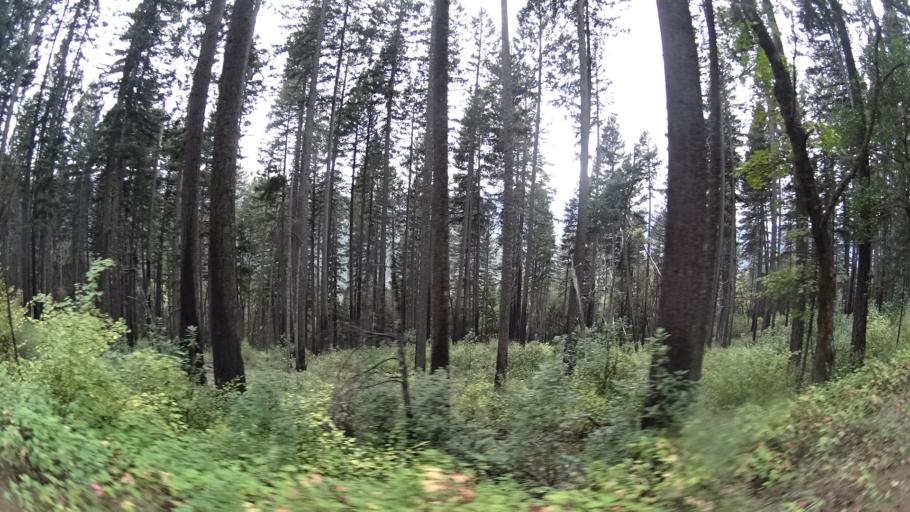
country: US
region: California
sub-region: Siskiyou County
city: Happy Camp
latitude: 41.8016
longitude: -123.3396
